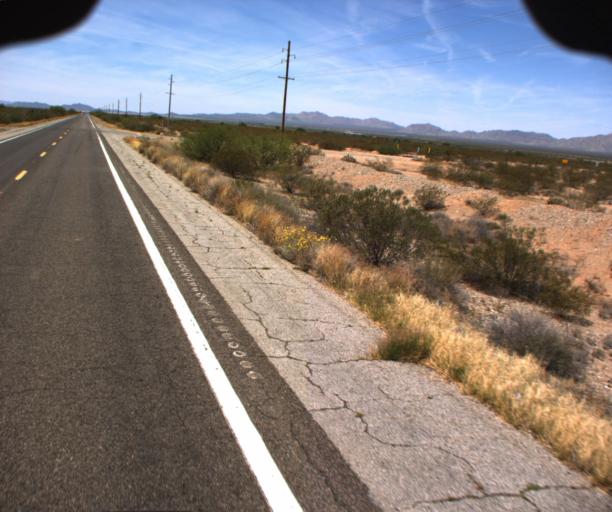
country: US
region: Arizona
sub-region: La Paz County
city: Salome
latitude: 33.8473
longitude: -113.4595
